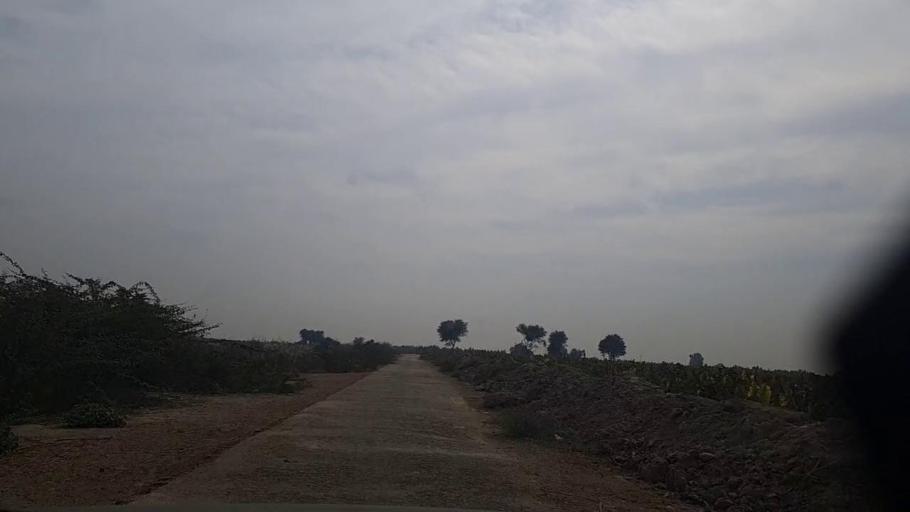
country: PK
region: Sindh
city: Sakrand
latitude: 26.2429
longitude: 68.2957
